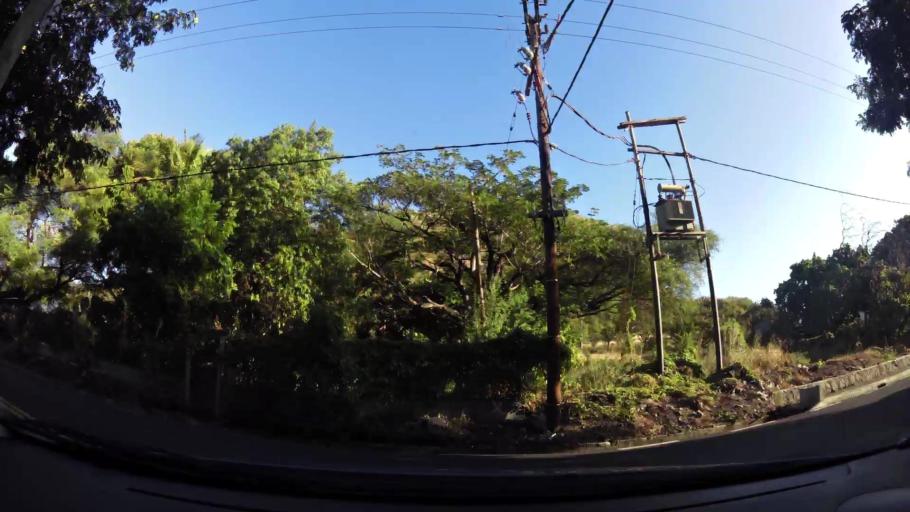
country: MU
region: Port Louis
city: Port Louis
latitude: -20.1672
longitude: 57.4931
